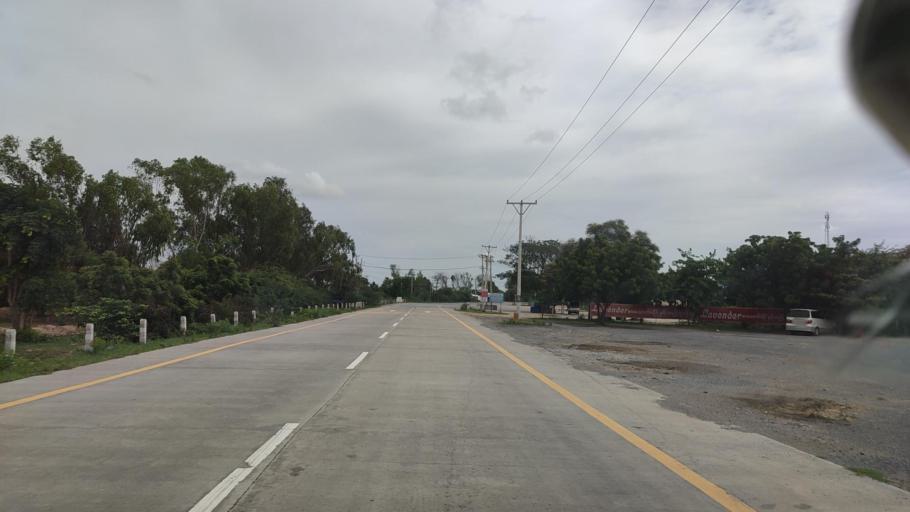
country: MM
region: Mandalay
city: Meiktila
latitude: 21.1225
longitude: 96.0275
